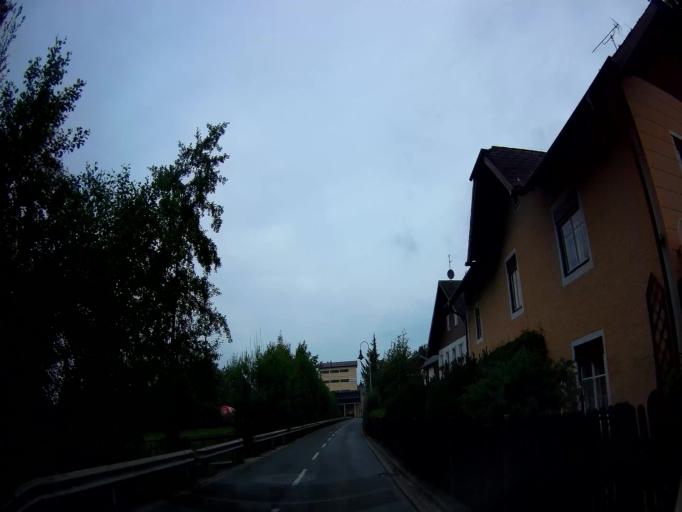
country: AT
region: Salzburg
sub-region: Politischer Bezirk Salzburg-Umgebung
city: Mattsee
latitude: 48.0970
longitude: 13.1497
